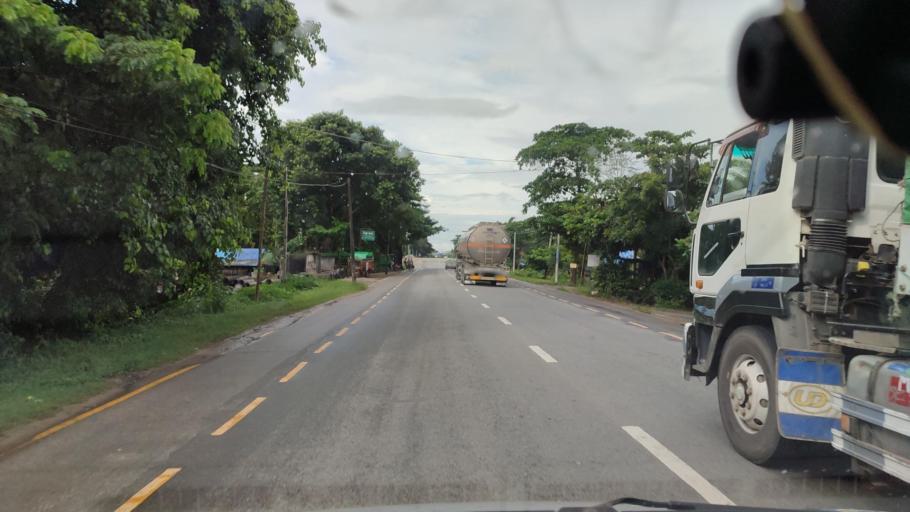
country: MM
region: Bago
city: Nyaunglebin
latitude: 17.8005
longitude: 96.6666
